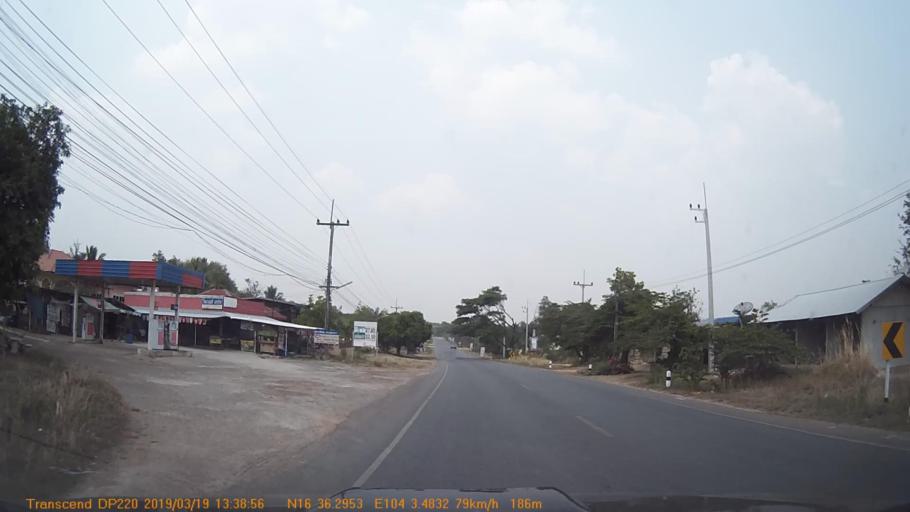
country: TH
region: Kalasin
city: Kuchinarai
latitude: 16.6053
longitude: 104.0581
